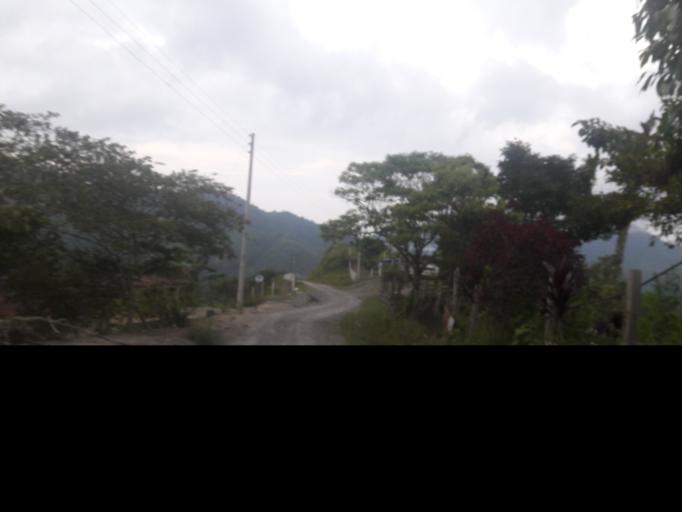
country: CO
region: Boyaca
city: Quipama
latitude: 5.5810
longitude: -74.2153
